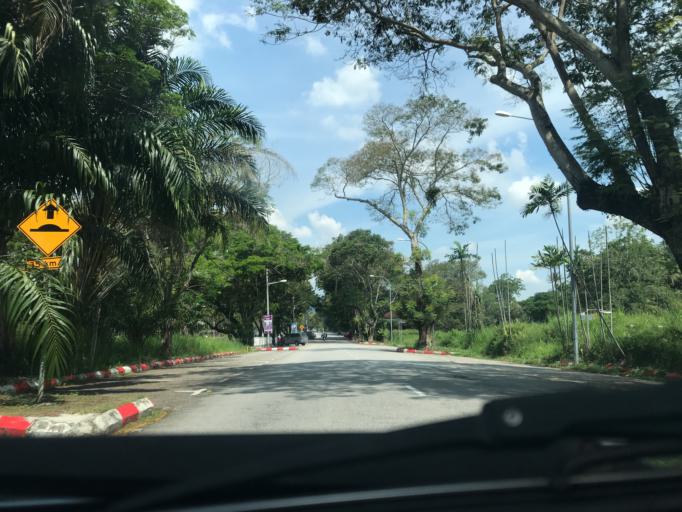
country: MY
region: Perak
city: Ipoh
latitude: 4.5980
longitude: 101.1087
